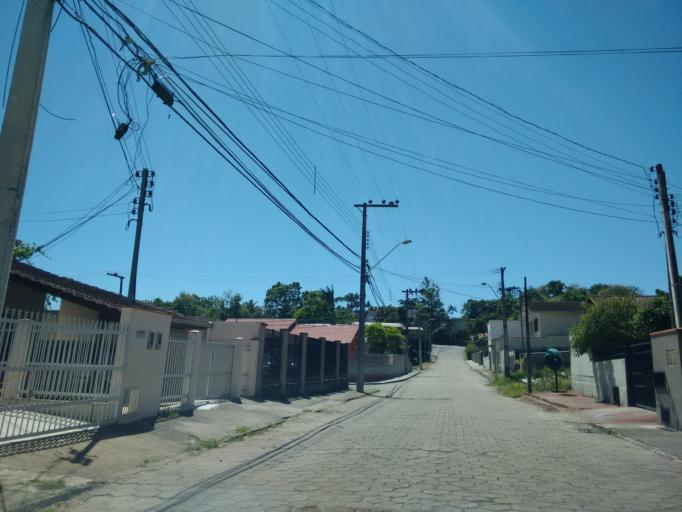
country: BR
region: Santa Catarina
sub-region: Blumenau
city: Blumenau
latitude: -26.8931
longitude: -49.1045
